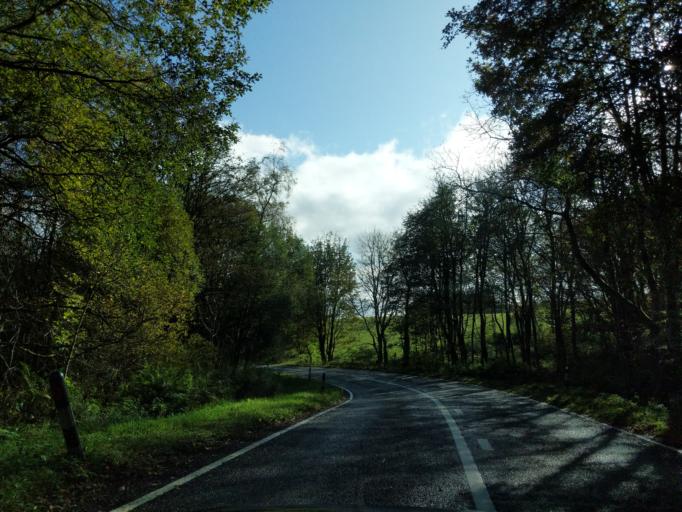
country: GB
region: Scotland
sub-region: Dumfries and Galloway
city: Moffat
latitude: 55.3414
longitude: -3.4588
